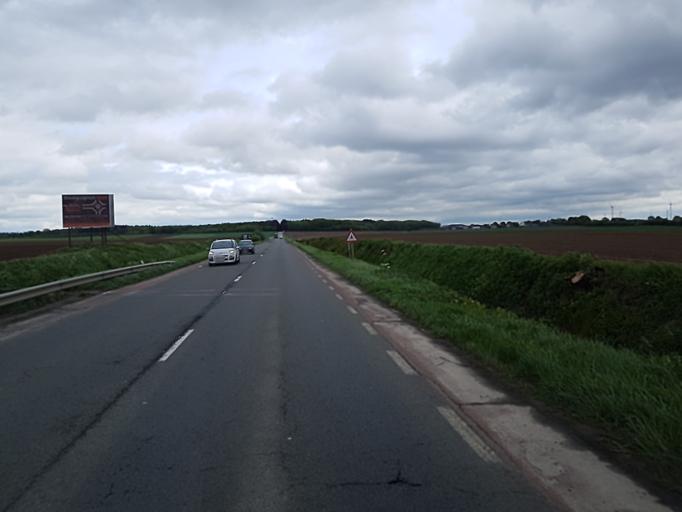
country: BE
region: Wallonia
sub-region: Province du Brabant Wallon
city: Walhain-Saint-Paul
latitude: 50.5974
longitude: 4.7297
